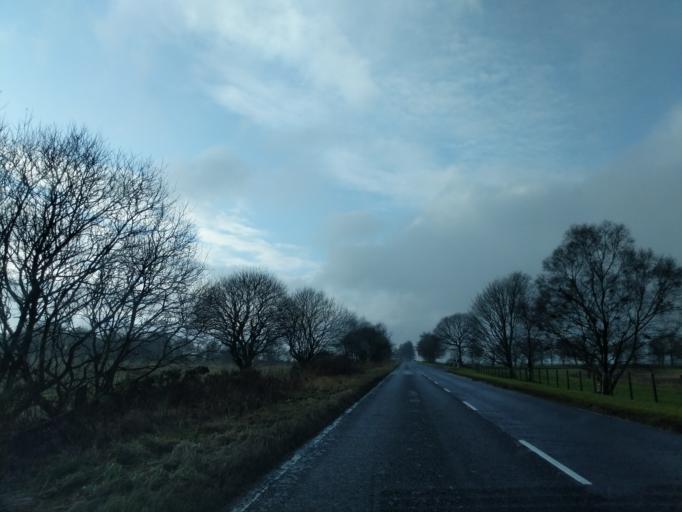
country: GB
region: Scotland
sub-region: Perth and Kinross
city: Kinross
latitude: 56.1977
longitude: -3.5105
